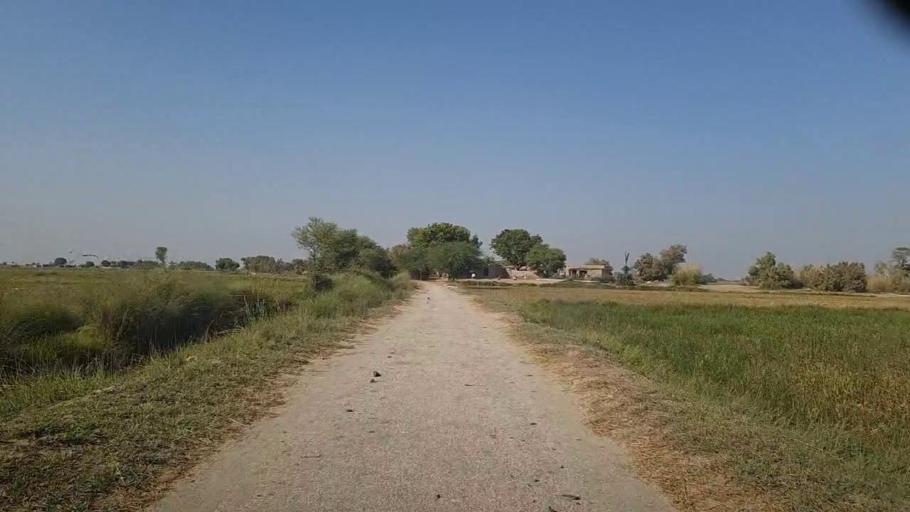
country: PK
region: Sindh
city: Tangwani
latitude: 28.2576
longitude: 68.9369
